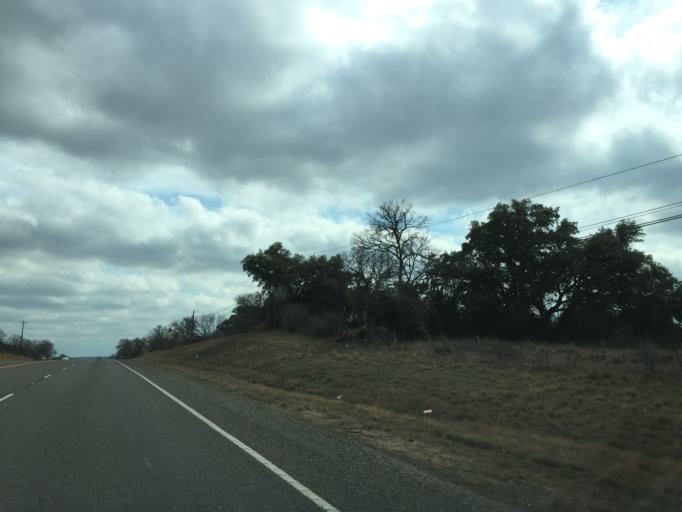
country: US
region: Texas
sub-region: Burnet County
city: Marble Falls
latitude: 30.4801
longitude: -98.1954
